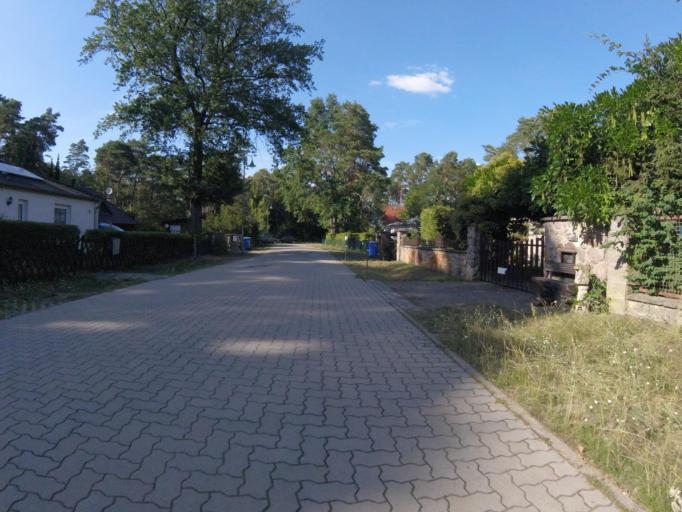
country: DE
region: Brandenburg
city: Wildau
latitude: 52.3131
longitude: 13.6975
